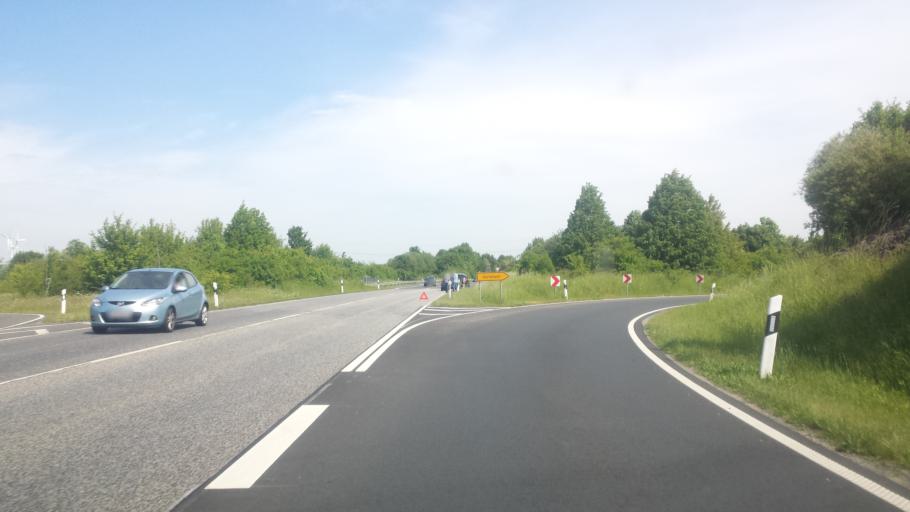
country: DE
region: Hesse
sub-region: Regierungsbezirk Darmstadt
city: Bad Vilbel
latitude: 50.2094
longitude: 8.7356
